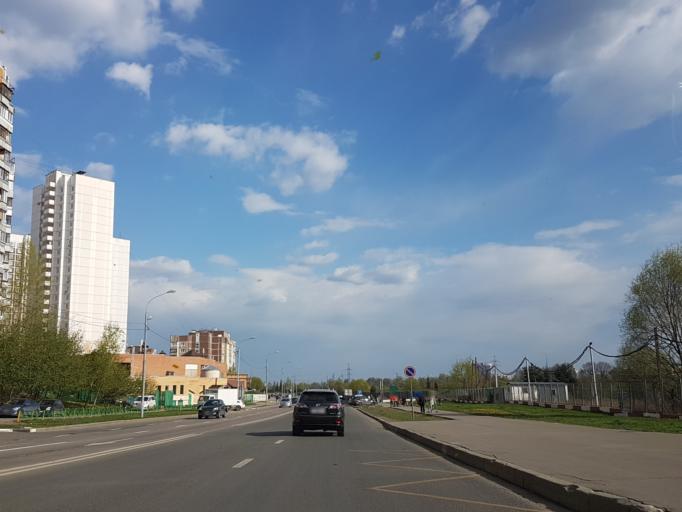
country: RU
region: Moskovskaya
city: Pavshino
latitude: 55.8421
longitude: 37.3547
